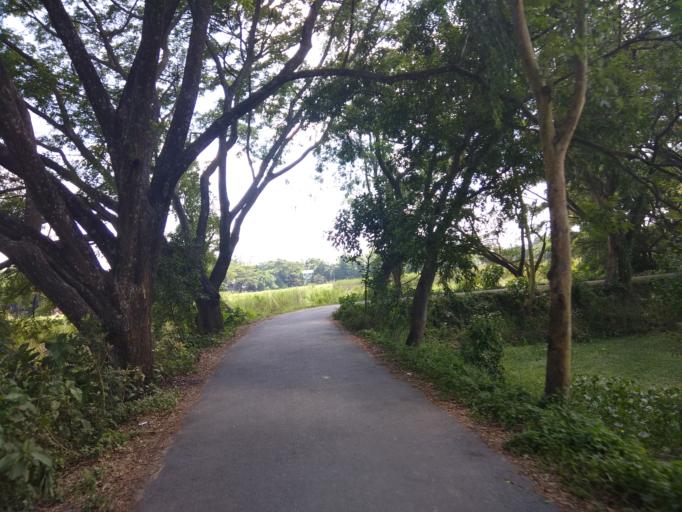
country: BD
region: Dhaka
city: Narayanganj
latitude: 23.4426
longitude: 90.4697
